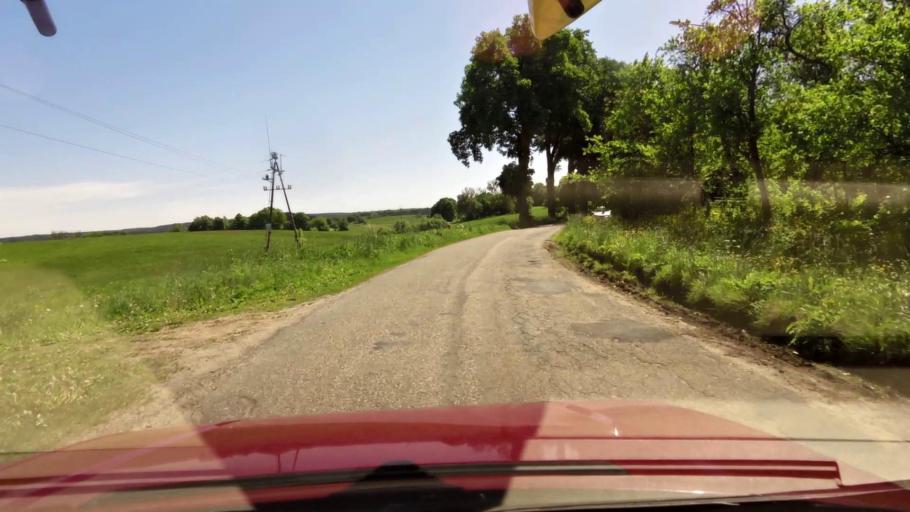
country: PL
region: West Pomeranian Voivodeship
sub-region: Powiat koszalinski
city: Bobolice
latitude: 54.0162
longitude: 16.6516
